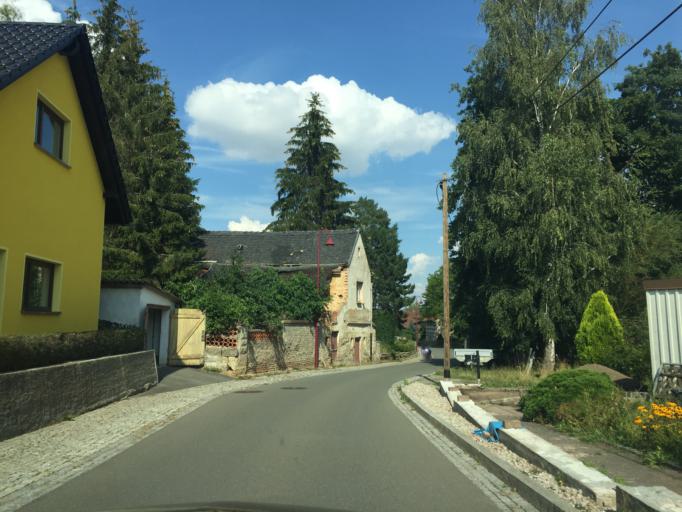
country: DE
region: Thuringia
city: Vollmershain
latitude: 50.8643
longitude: 12.3133
